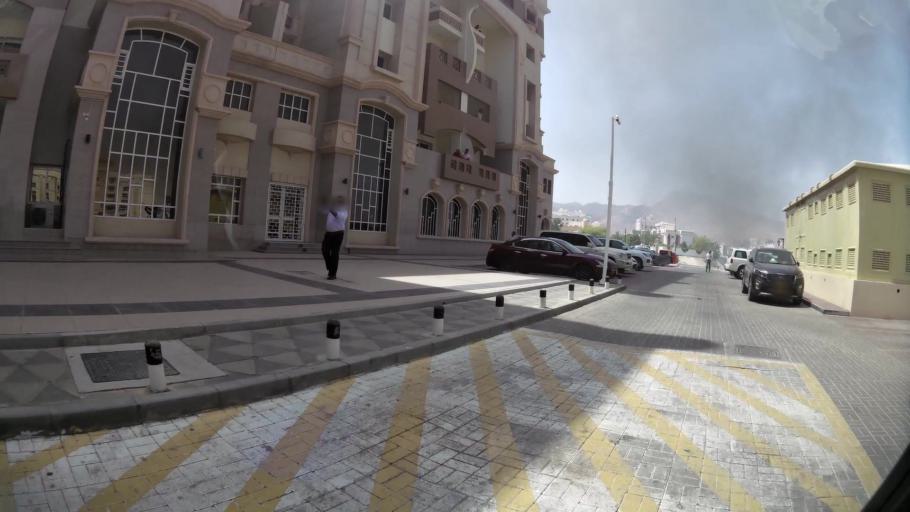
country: OM
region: Muhafazat Masqat
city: Bawshar
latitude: 23.5860
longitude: 58.4218
